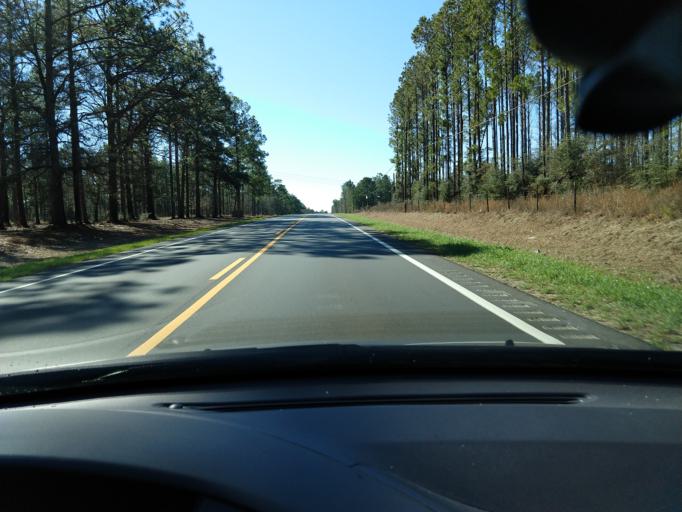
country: US
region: Alabama
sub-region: Covington County
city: Andalusia
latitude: 31.2202
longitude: -86.5332
